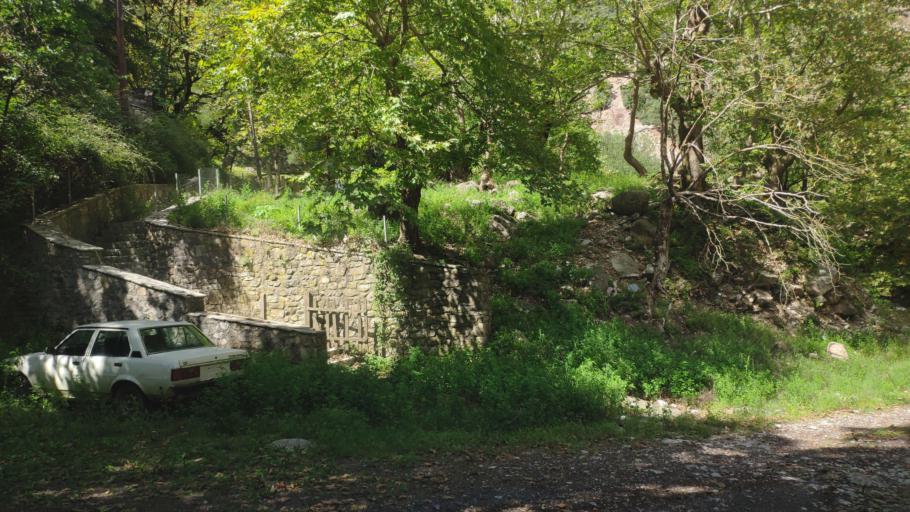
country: GR
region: Central Greece
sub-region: Nomos Evrytanias
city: Kerasochori
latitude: 39.1236
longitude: 21.6550
